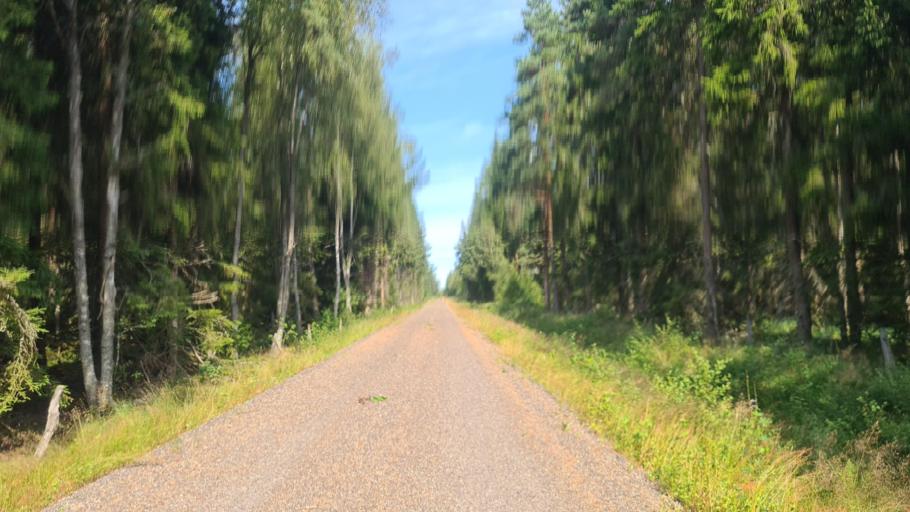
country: SE
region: Kronoberg
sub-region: Ljungby Kommun
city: Lagan
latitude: 56.9785
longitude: 13.9471
